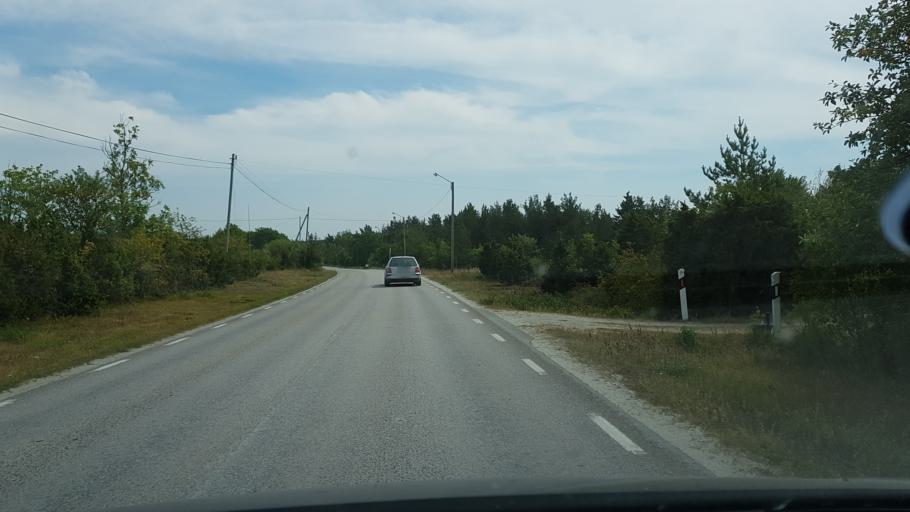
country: SE
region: Gotland
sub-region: Gotland
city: Slite
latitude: 57.7326
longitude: 18.7407
